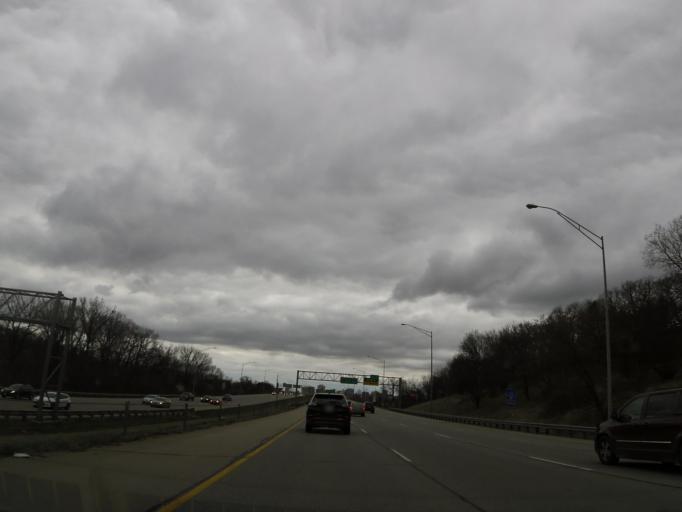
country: US
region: Iowa
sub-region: Linn County
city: Cedar Rapids
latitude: 42.0039
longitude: -91.6666
